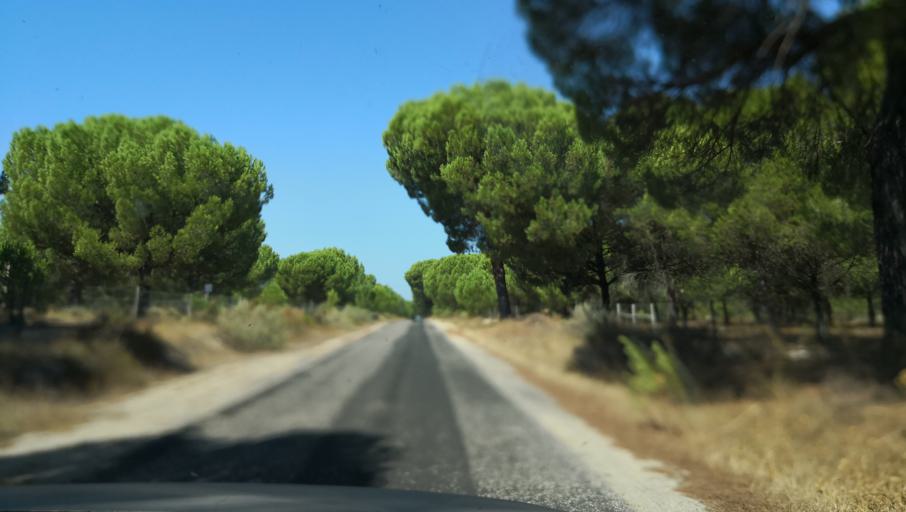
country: PT
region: Setubal
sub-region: Alcacer do Sal
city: Alcacer do Sal
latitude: 38.2575
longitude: -8.3044
